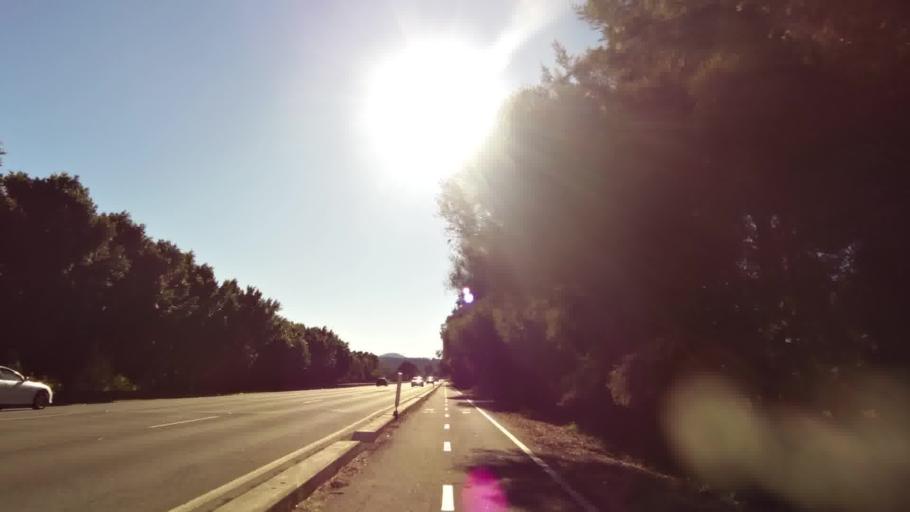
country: AU
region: New South Wales
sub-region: Wollongong
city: Koonawarra
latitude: -34.4857
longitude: 150.8002
